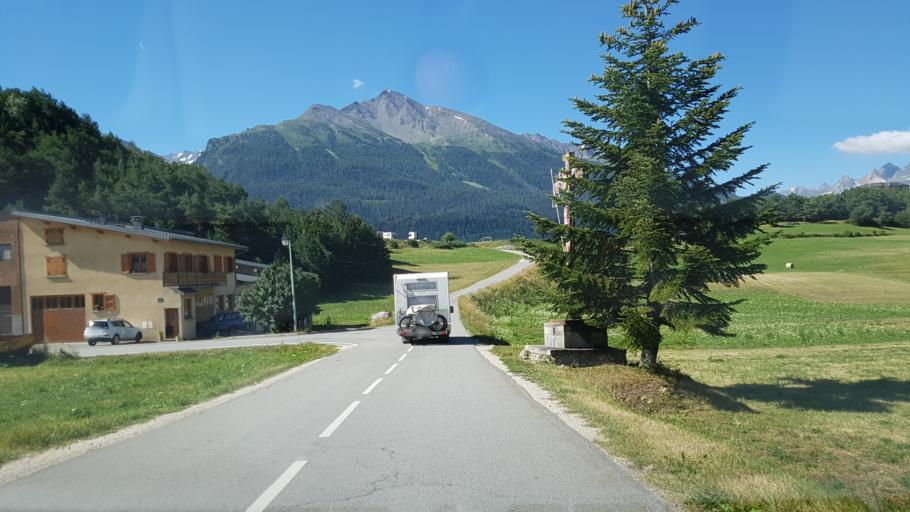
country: FR
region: Rhone-Alpes
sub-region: Departement de la Savoie
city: Modane
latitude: 45.2239
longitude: 6.7406
